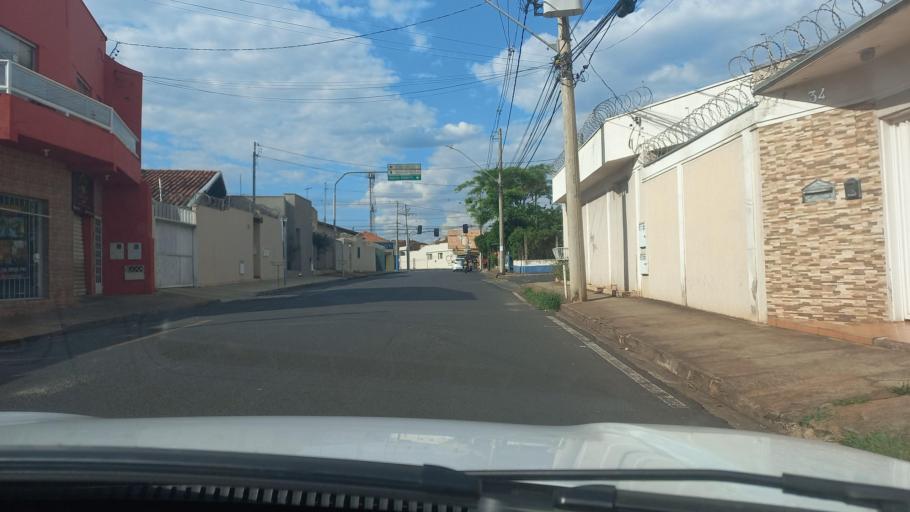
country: BR
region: Minas Gerais
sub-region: Uberaba
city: Uberaba
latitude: -19.7350
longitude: -47.9242
